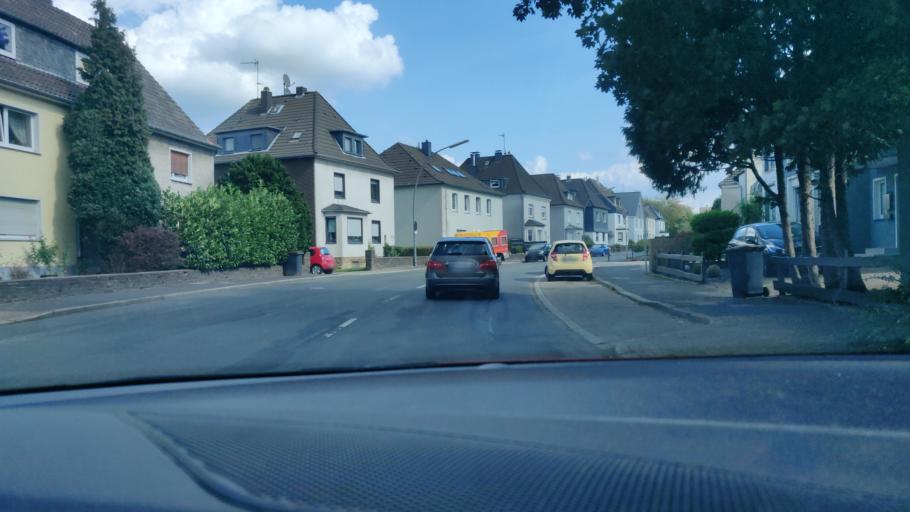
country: DE
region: North Rhine-Westphalia
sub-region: Regierungsbezirk Dusseldorf
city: Velbert
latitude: 51.3477
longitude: 7.0423
